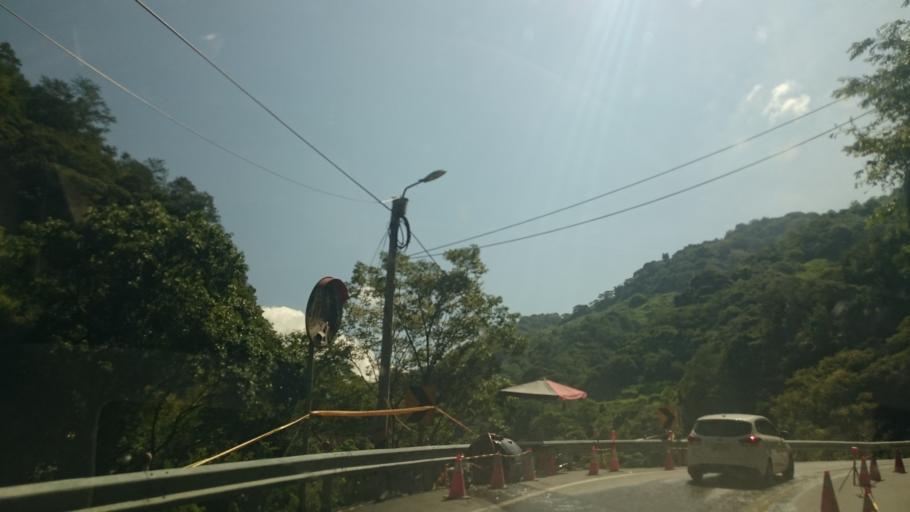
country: TW
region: Taiwan
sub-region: Nantou
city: Puli
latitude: 24.0090
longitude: 121.1130
